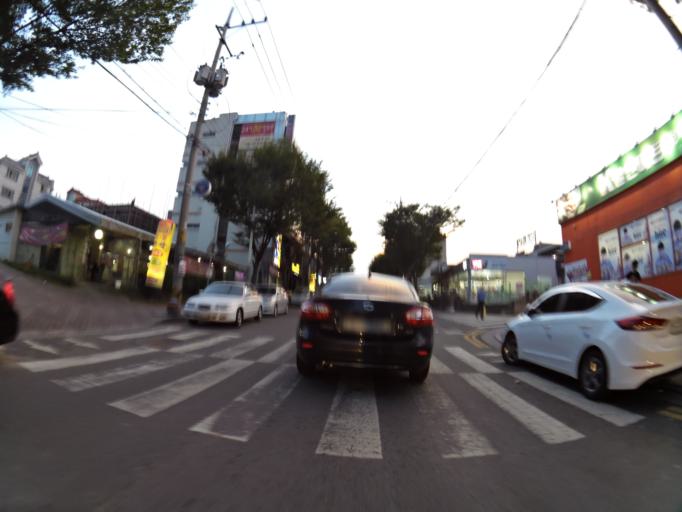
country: KR
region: Gyeongsangbuk-do
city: Gyeongsan-si
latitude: 35.8425
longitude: 128.7507
